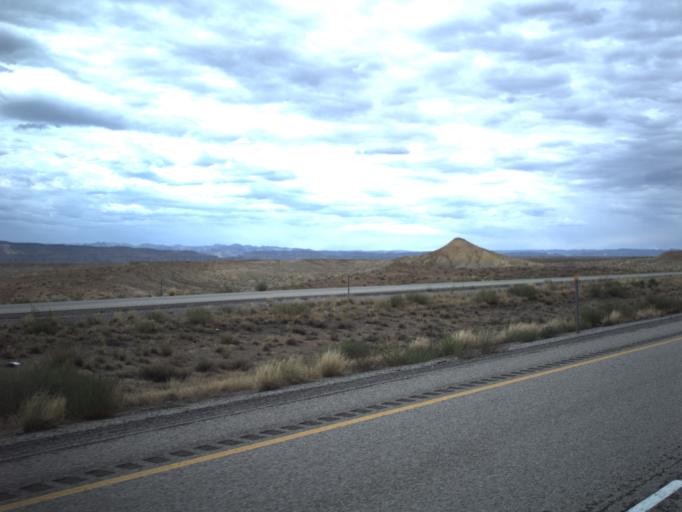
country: US
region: Utah
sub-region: Grand County
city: Moab
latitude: 38.9481
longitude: -109.3946
